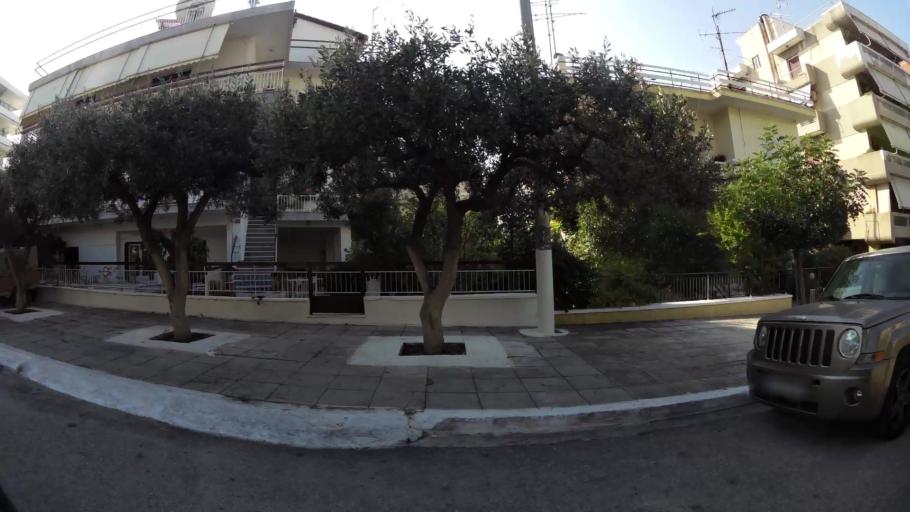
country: GR
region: Attica
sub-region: Nomarchia Athinas
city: Argyroupoli
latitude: 37.9214
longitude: 23.7520
